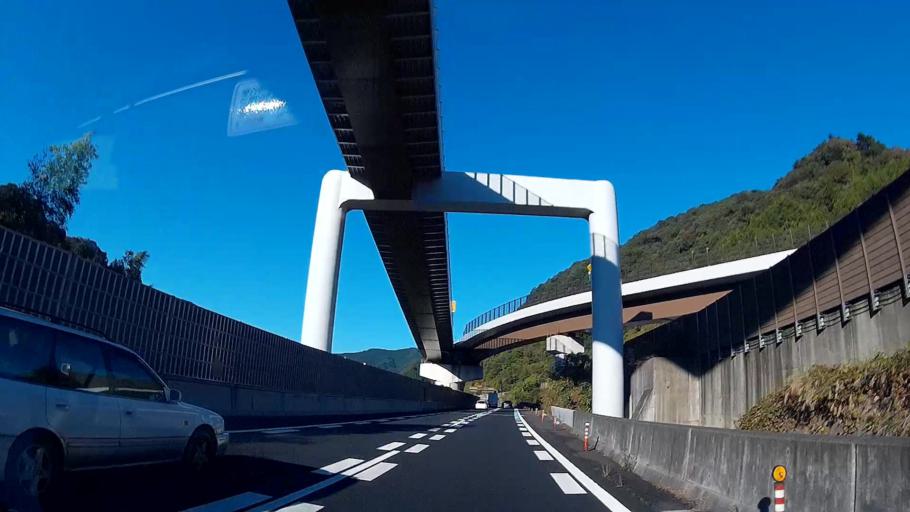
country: JP
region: Tokyo
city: Hachioji
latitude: 35.6404
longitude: 139.2527
